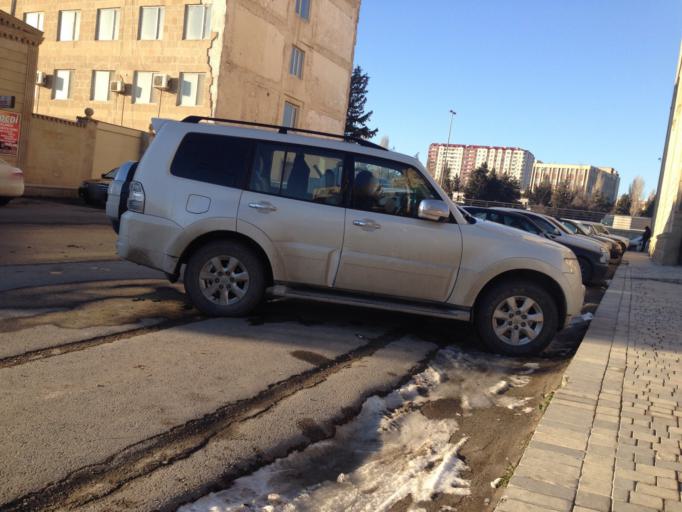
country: AZ
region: Baki
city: Baku
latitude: 40.4145
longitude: 49.8558
